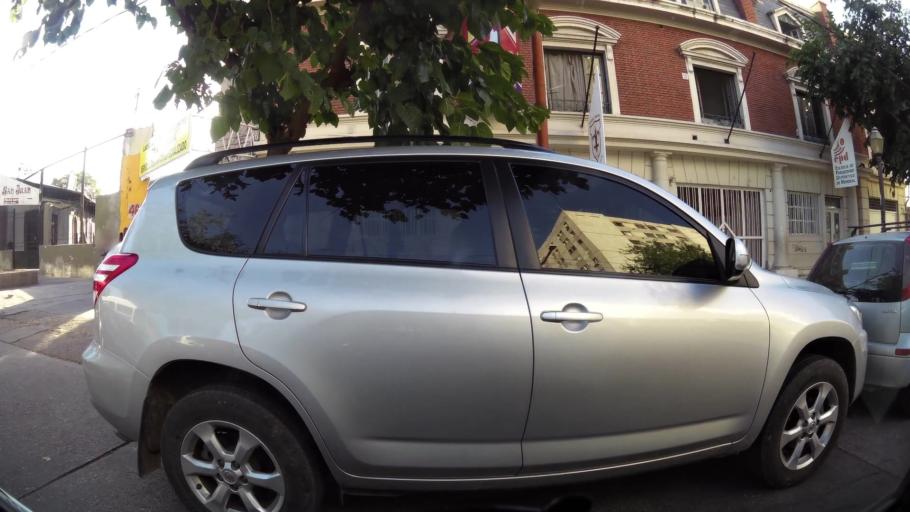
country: AR
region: Mendoza
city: Mendoza
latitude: -32.8984
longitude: -68.8394
